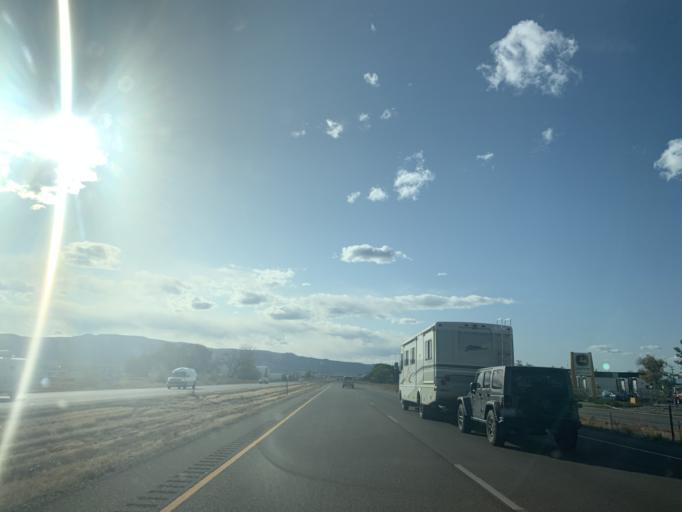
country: US
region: Colorado
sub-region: Mesa County
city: Redlands
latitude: 39.1140
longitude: -108.6139
